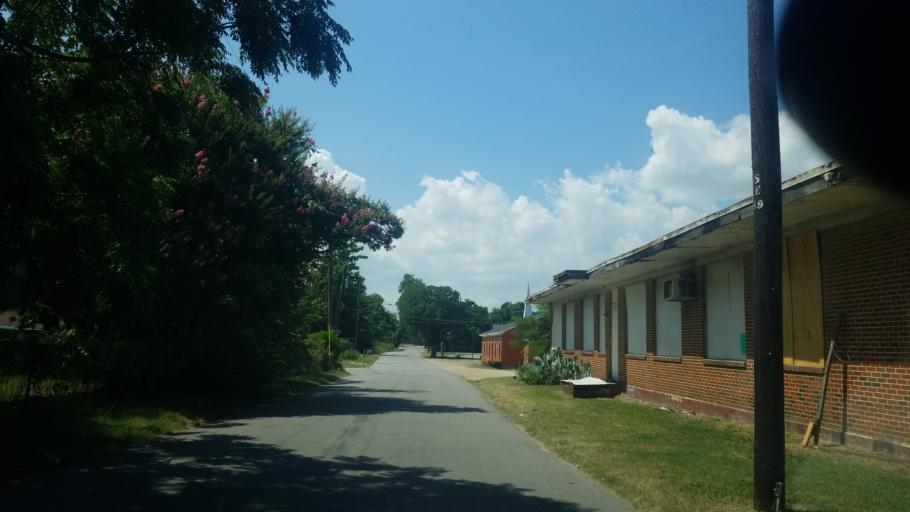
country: US
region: Texas
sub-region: Dallas County
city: Hutchins
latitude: 32.7153
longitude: -96.7480
